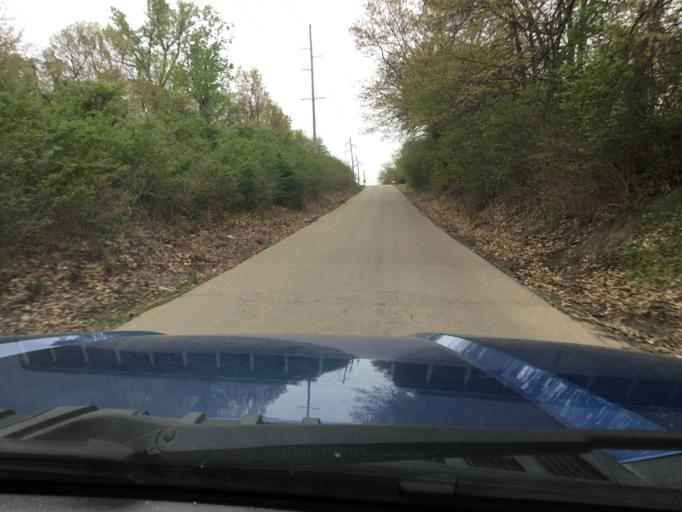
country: US
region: Kansas
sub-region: Shawnee County
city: Topeka
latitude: 39.1041
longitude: -95.6874
